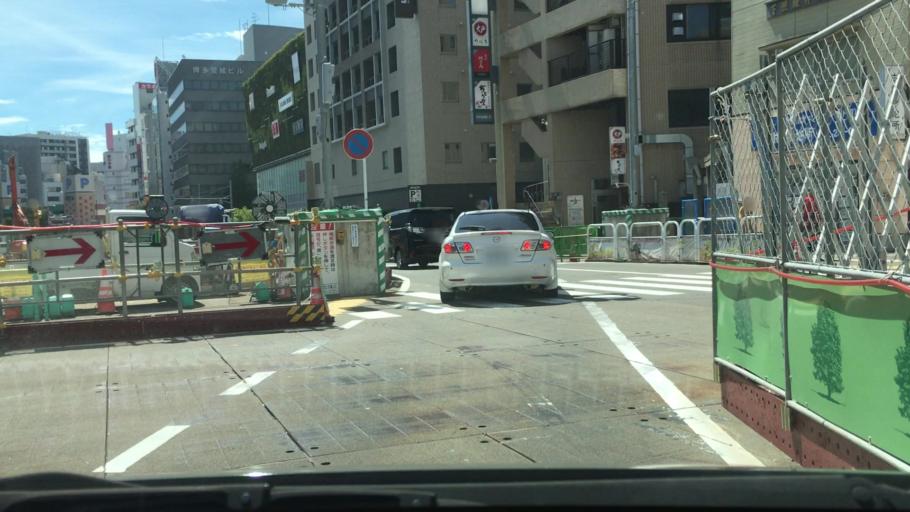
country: JP
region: Fukuoka
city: Fukuoka-shi
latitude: 33.5912
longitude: 130.4118
